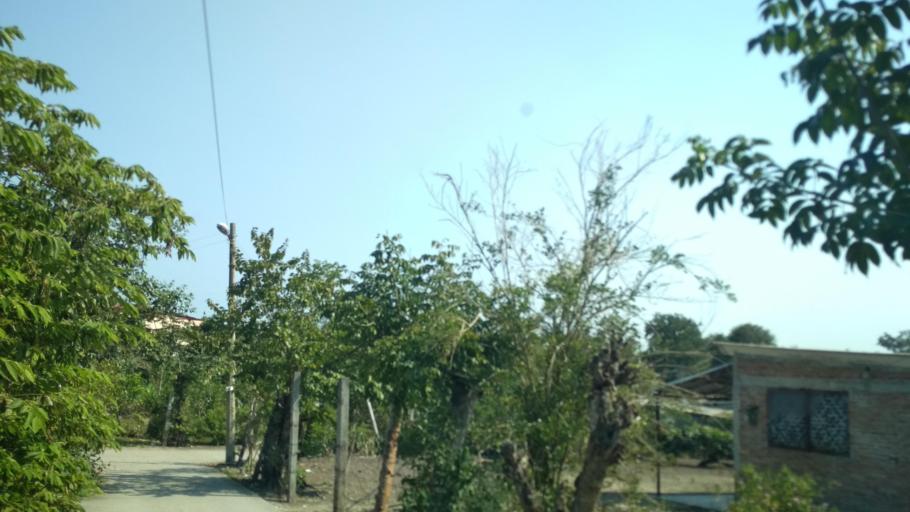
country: MX
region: Veracruz
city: Gutierrez Zamora
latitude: 20.4170
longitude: -97.1884
